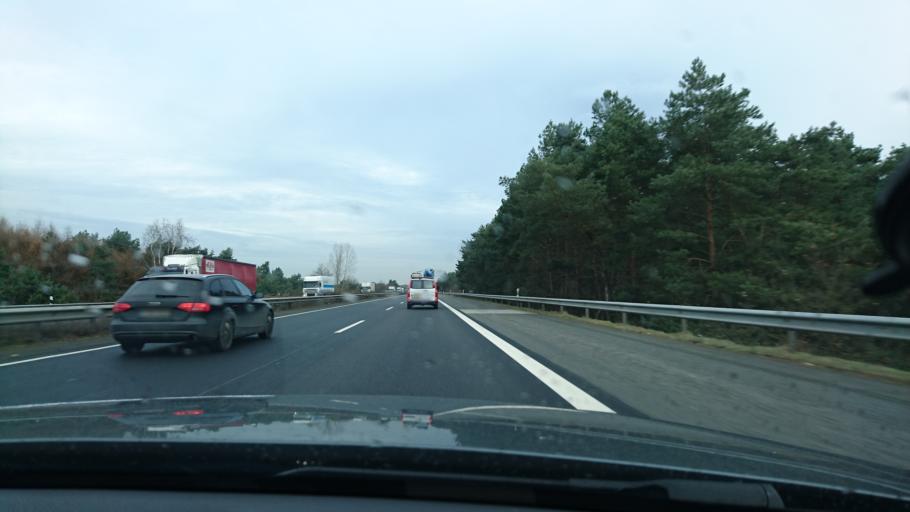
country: DE
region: Lower Saxony
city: Holdorf
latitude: 52.5647
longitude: 8.1122
